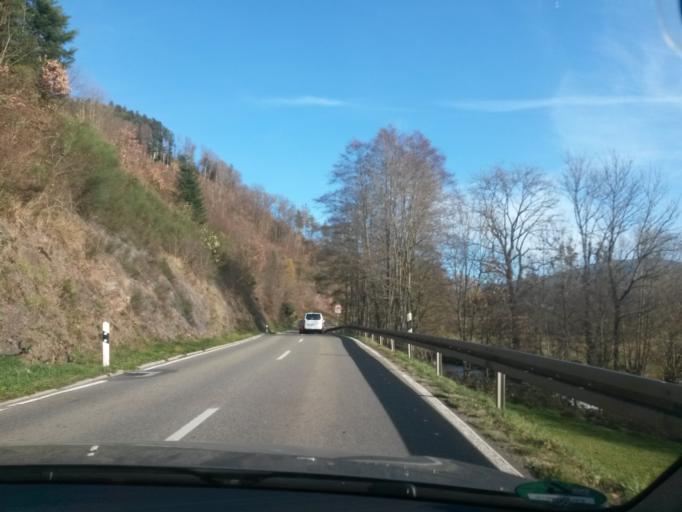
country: DE
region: Baden-Wuerttemberg
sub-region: Freiburg Region
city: Elzach
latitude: 48.1567
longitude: 8.0463
